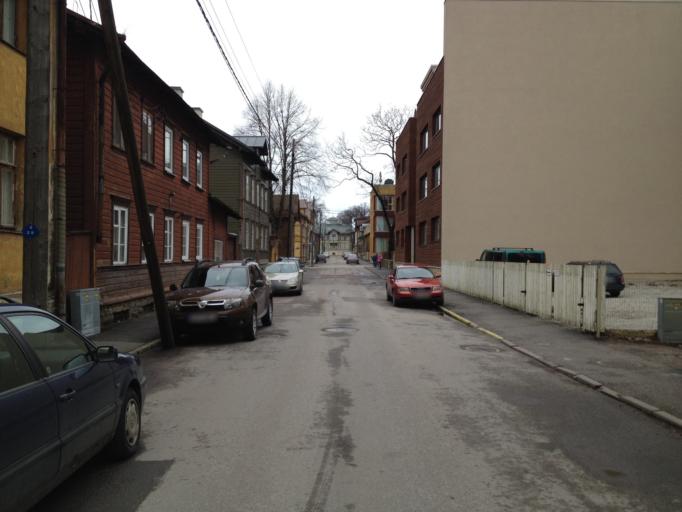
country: EE
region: Harju
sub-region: Tallinna linn
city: Tallinn
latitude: 59.4299
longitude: 24.7271
